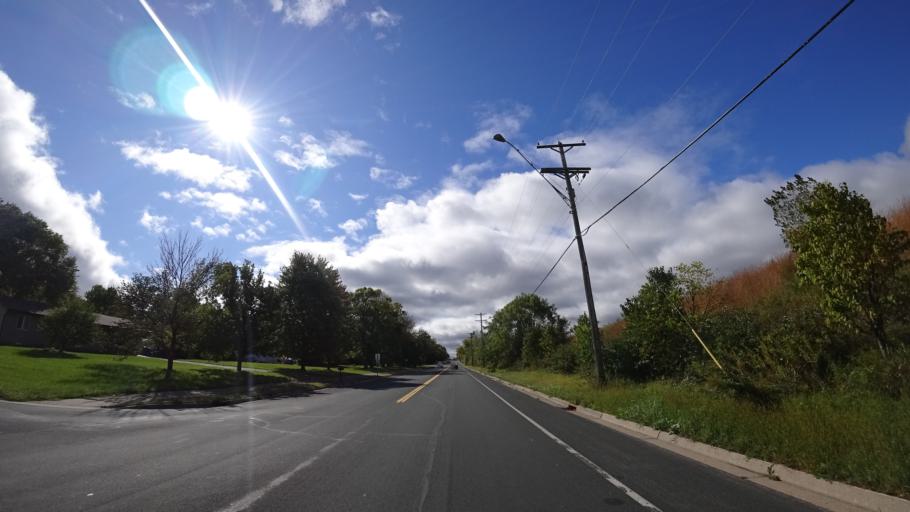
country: US
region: Minnesota
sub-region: Dakota County
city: Eagan
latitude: 44.8109
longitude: -93.2178
